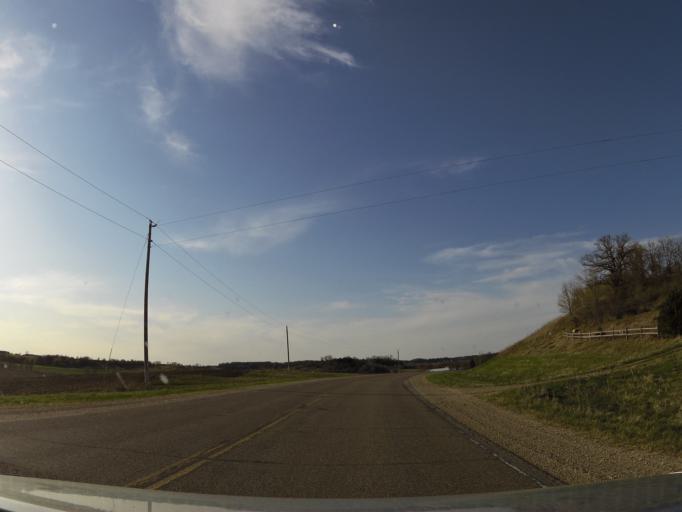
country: US
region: Wisconsin
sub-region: Pierce County
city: River Falls
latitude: 44.7901
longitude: -92.6463
